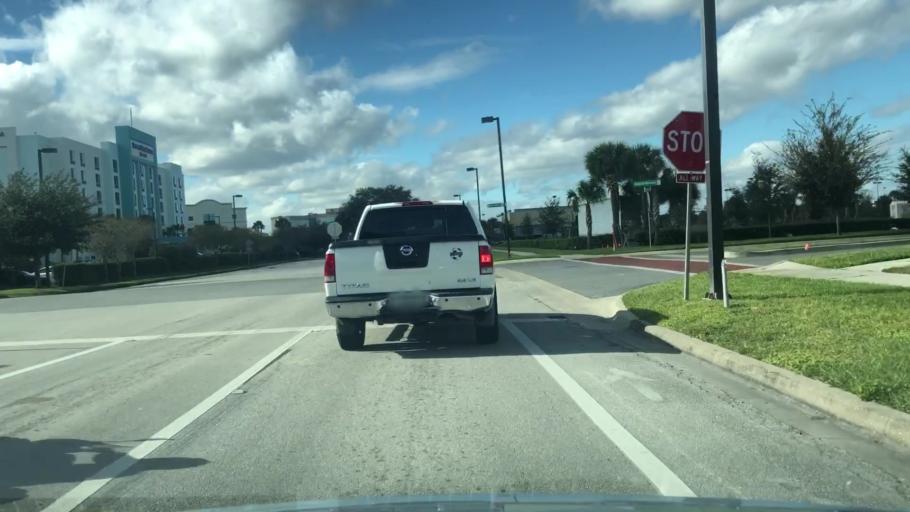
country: US
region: Florida
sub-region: Orange County
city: Conway
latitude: 28.4625
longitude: -81.3051
